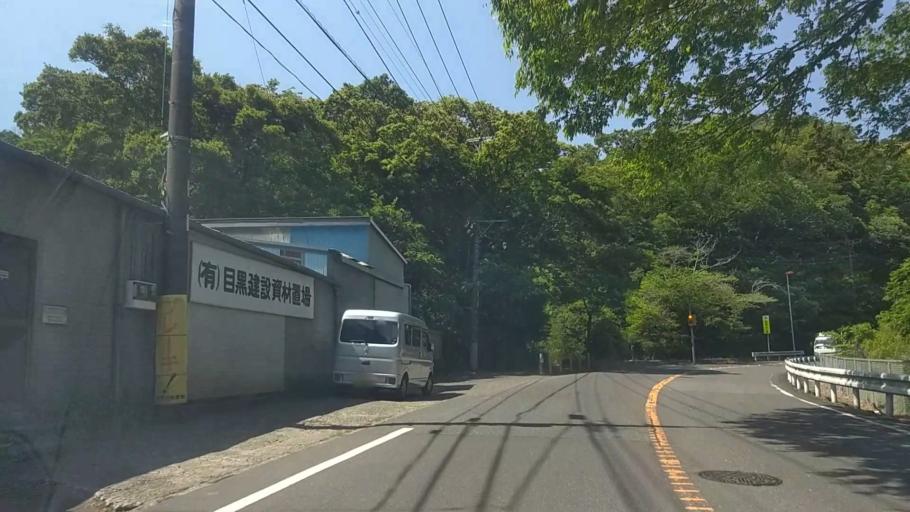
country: JP
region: Kanagawa
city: Zushi
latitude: 35.3129
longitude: 139.6005
